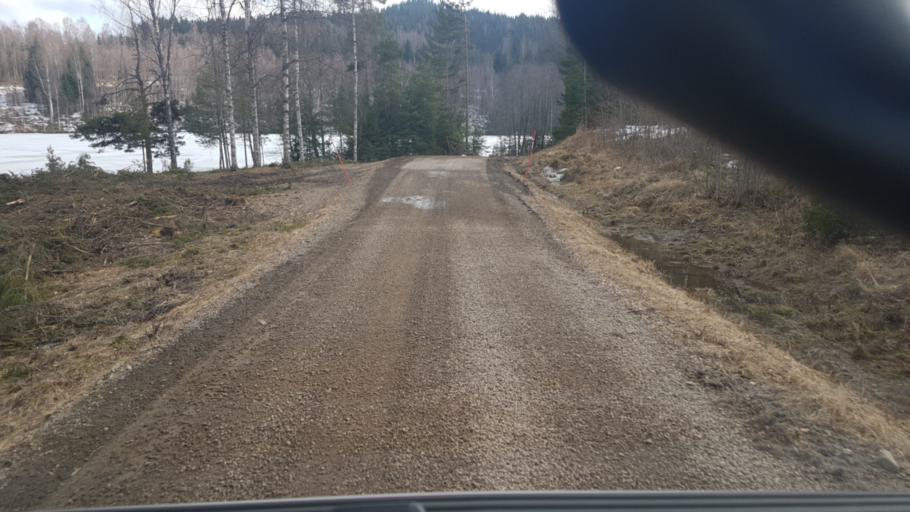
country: SE
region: Vaermland
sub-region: Eda Kommun
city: Amotfors
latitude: 59.8035
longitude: 12.4184
